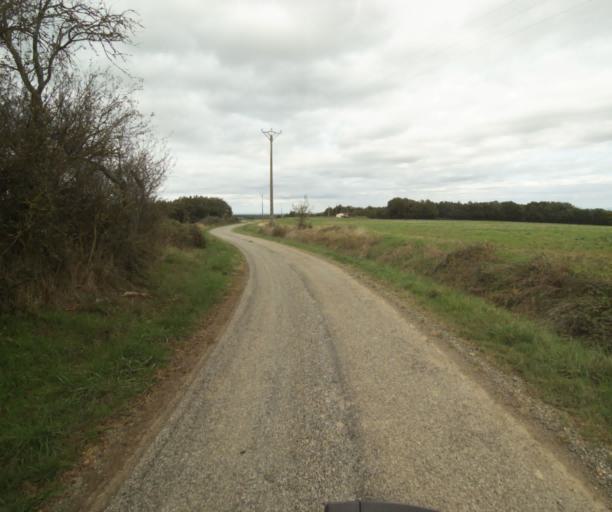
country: FR
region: Midi-Pyrenees
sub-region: Departement du Tarn-et-Garonne
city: Beaumont-de-Lomagne
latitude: 43.8488
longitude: 1.0968
